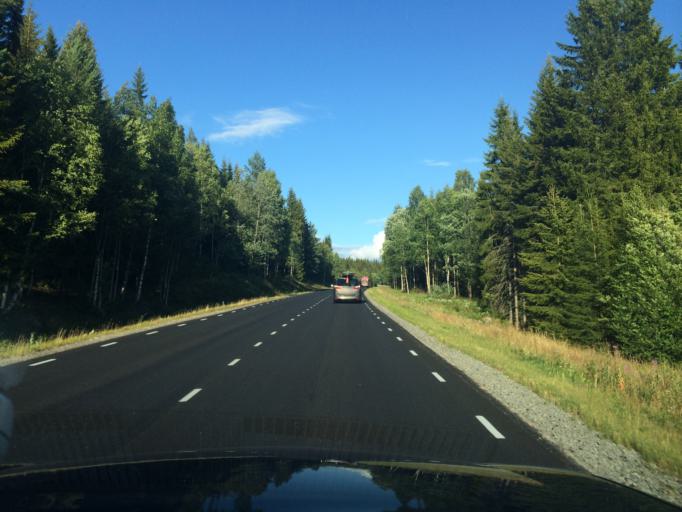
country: NO
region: Hedmark
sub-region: Elverum
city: Elverum
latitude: 61.0483
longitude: 11.8977
